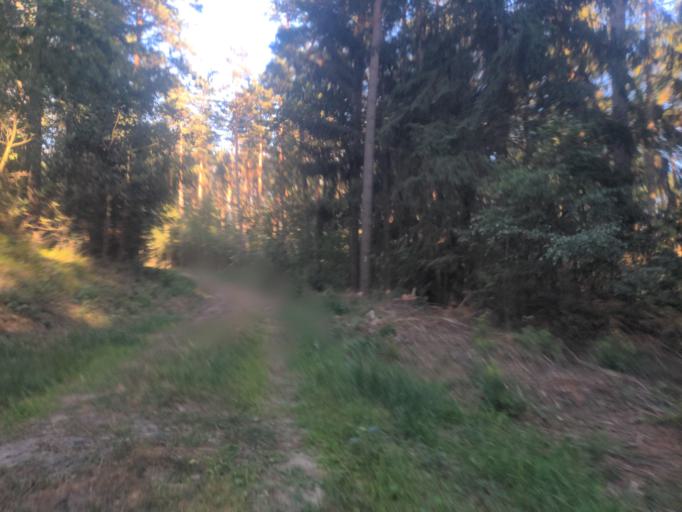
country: DE
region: Lower Saxony
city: Neu Darchau
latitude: 53.2139
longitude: 10.8705
